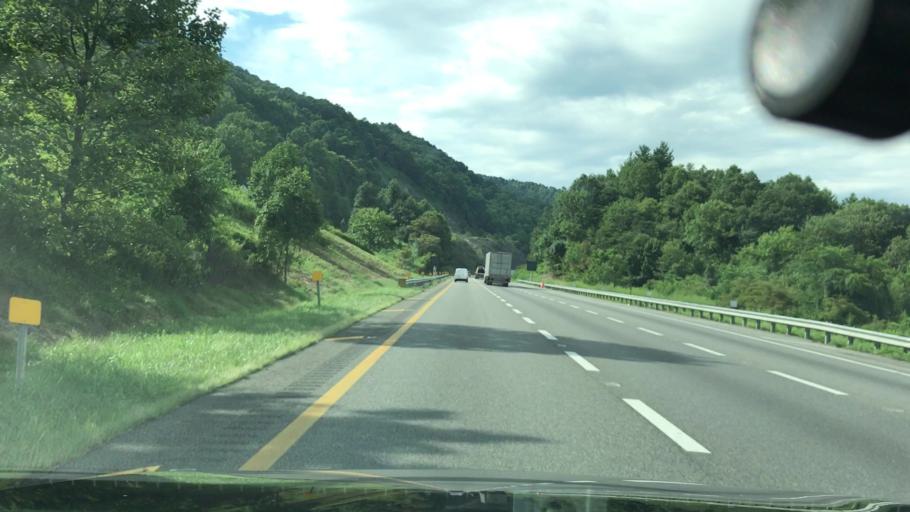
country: US
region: Virginia
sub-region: Carroll County
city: Cana
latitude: 36.6093
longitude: -80.7377
